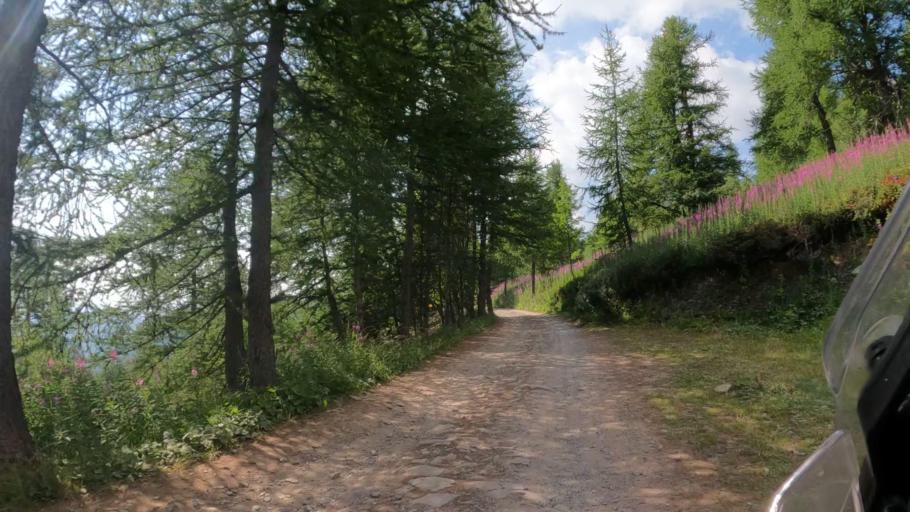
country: IT
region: Piedmont
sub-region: Provincia di Cuneo
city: Briga Alta
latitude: 44.1276
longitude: 7.6910
